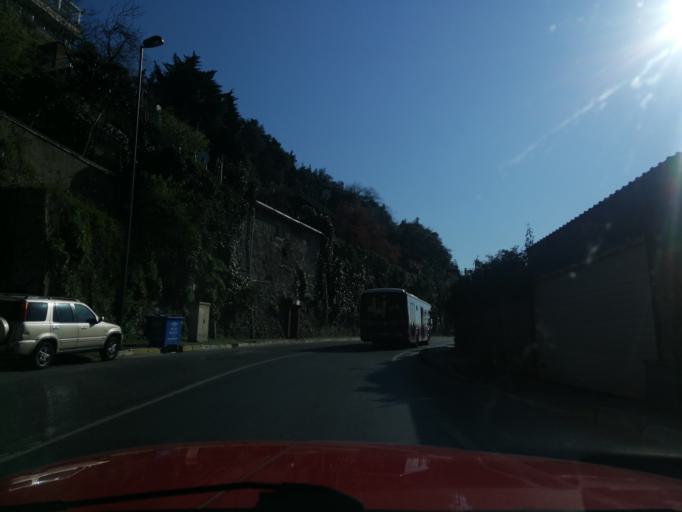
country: TR
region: Istanbul
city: UEskuedar
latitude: 41.0632
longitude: 29.0550
